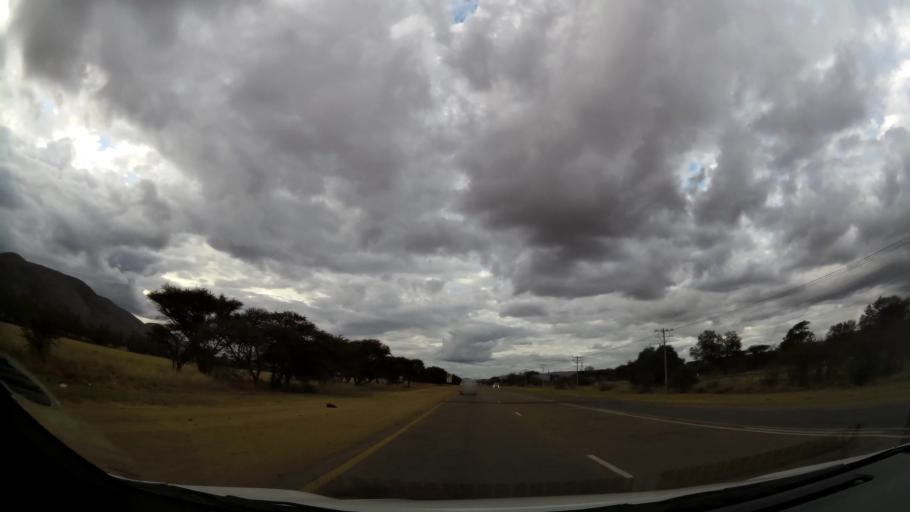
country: ZA
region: Limpopo
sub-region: Waterberg District Municipality
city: Mokopane
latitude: -24.2698
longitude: 28.9816
